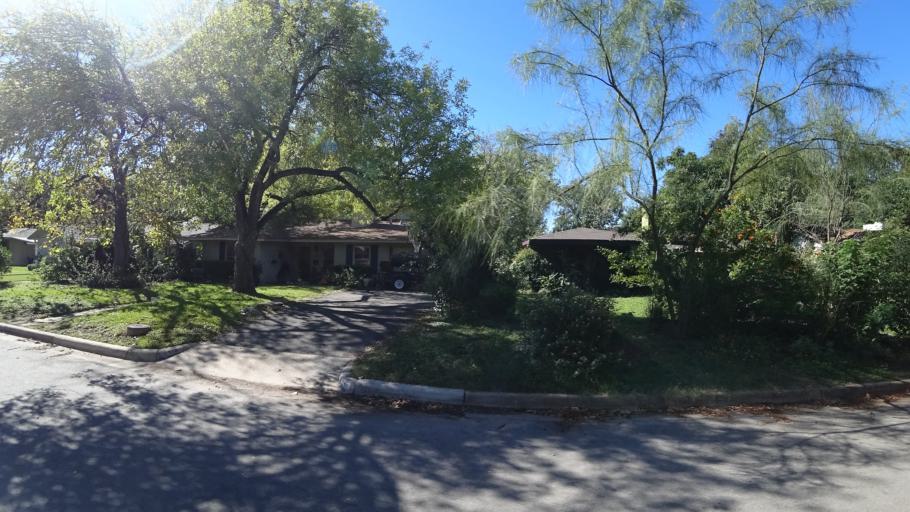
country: US
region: Texas
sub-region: Travis County
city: Austin
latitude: 30.3012
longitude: -97.7098
